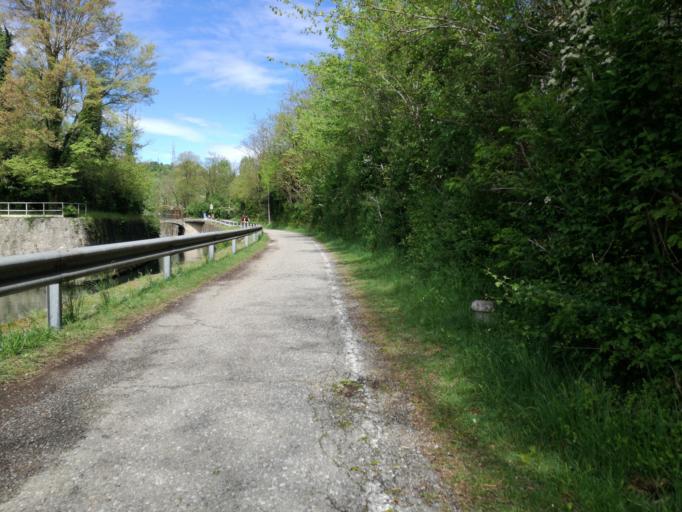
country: IT
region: Lombardy
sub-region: Provincia di Monza e Brianza
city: Porto d'Adda
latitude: 45.6660
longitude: 9.4852
